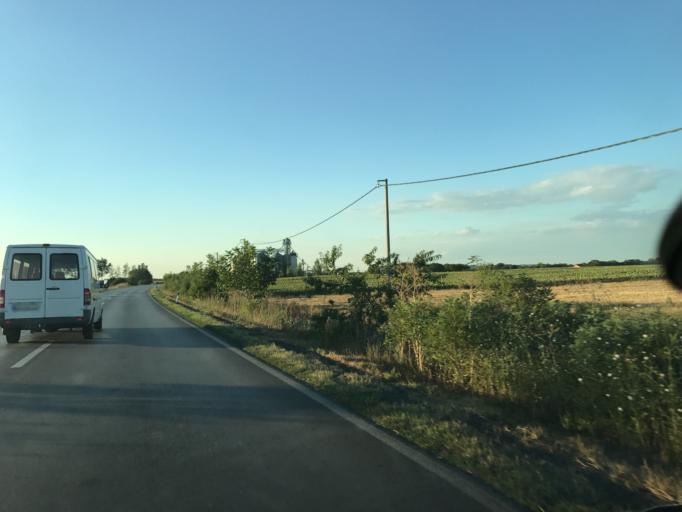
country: RS
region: Central Serbia
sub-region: Branicevski Okrug
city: Pozarevac
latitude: 44.6250
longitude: 21.1450
